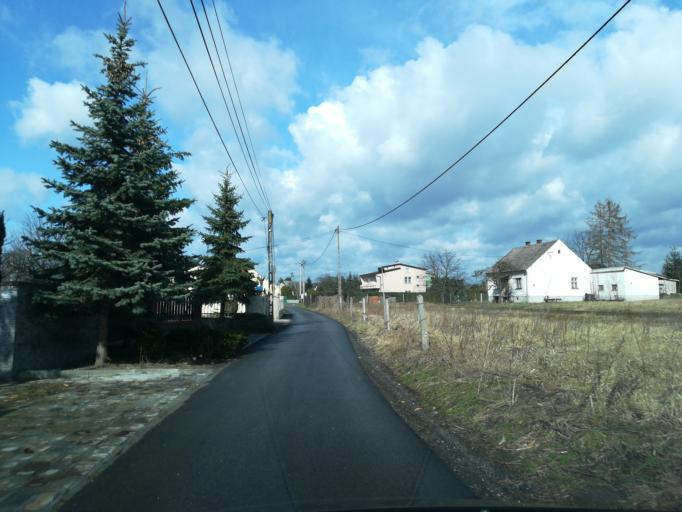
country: PL
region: Lesser Poland Voivodeship
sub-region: Powiat krakowski
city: Liszki
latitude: 50.0532
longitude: 19.7785
